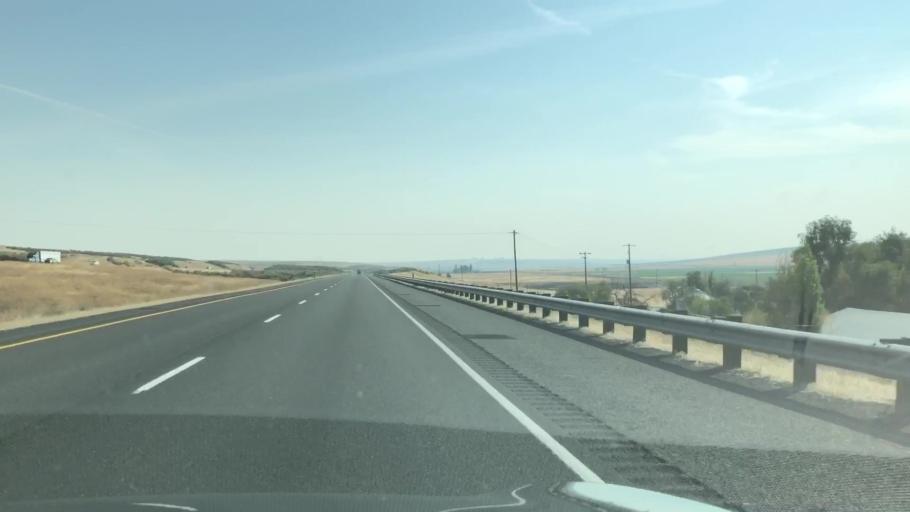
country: US
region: Washington
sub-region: Grant County
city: Warden
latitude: 47.0853
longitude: -118.9422
